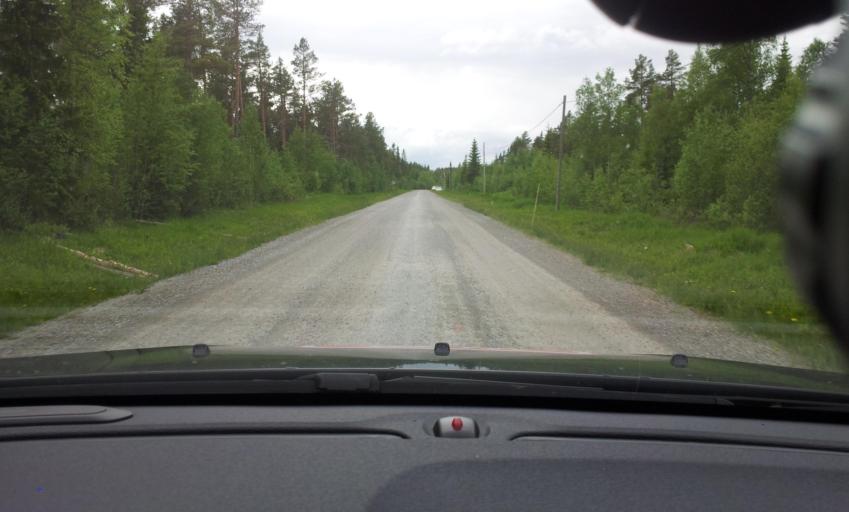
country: SE
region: Jaemtland
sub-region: OEstersunds Kommun
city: Brunflo
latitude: 63.0940
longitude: 14.9018
